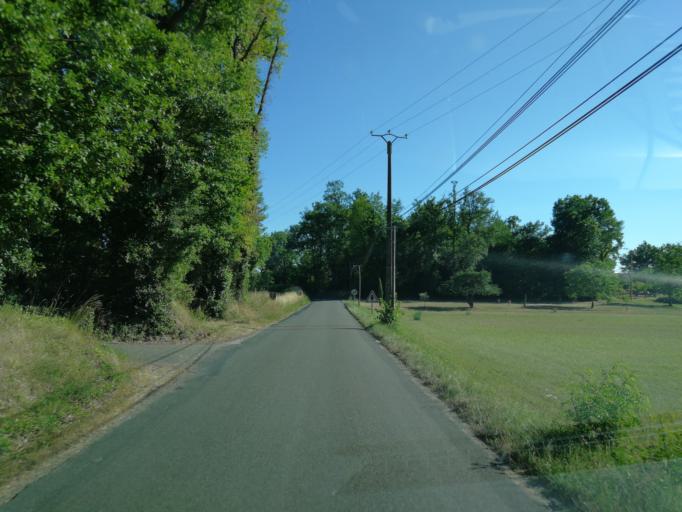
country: FR
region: Midi-Pyrenees
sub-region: Departement du Lot
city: Gourdon
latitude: 44.7558
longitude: 1.3759
